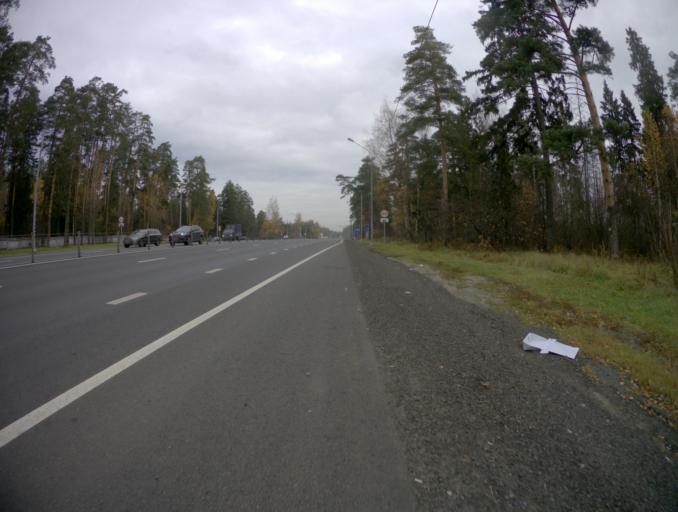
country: RU
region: Moskovskaya
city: Malaya Dubna
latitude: 55.8467
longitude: 38.9648
